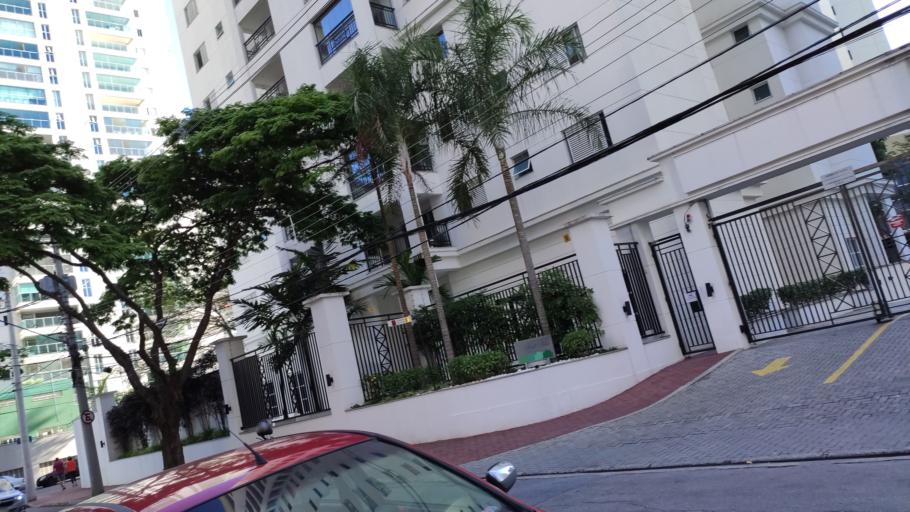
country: BR
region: Sao Paulo
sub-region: Sao Jose Dos Campos
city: Sao Jose dos Campos
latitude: -23.2159
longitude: -45.9083
